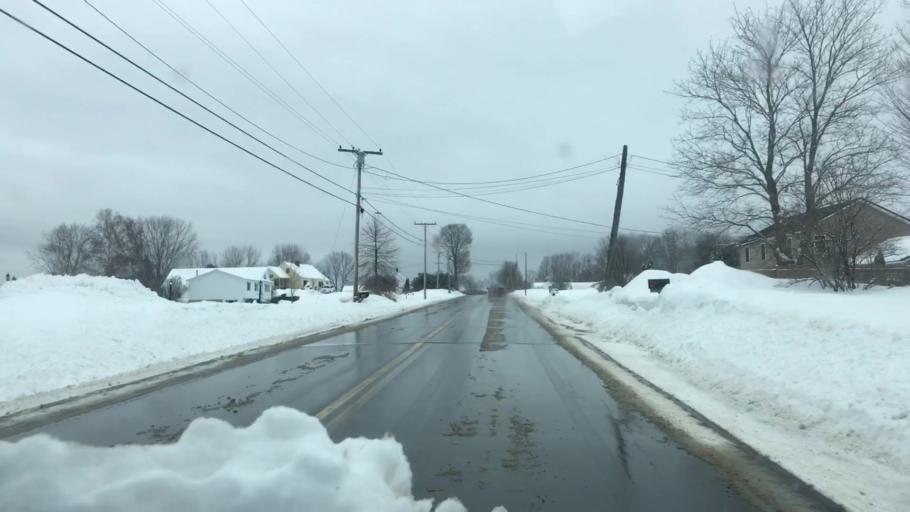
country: US
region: Maine
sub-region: Penobscot County
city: Charleston
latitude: 44.9957
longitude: -69.0485
